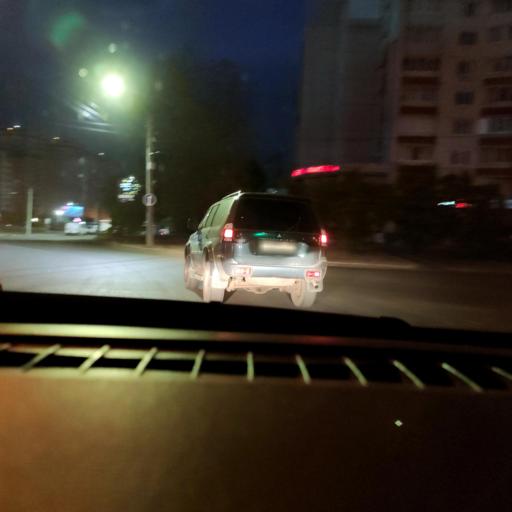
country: RU
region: Voronezj
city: Podgornoye
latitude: 51.7122
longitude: 39.1628
